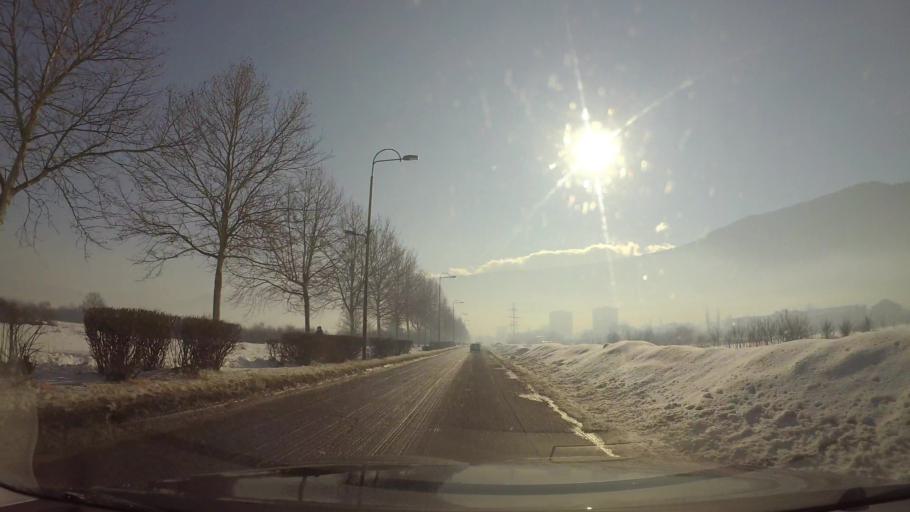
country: BA
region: Federation of Bosnia and Herzegovina
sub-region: Kanton Sarajevo
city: Sarajevo
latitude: 43.8030
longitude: 18.3123
